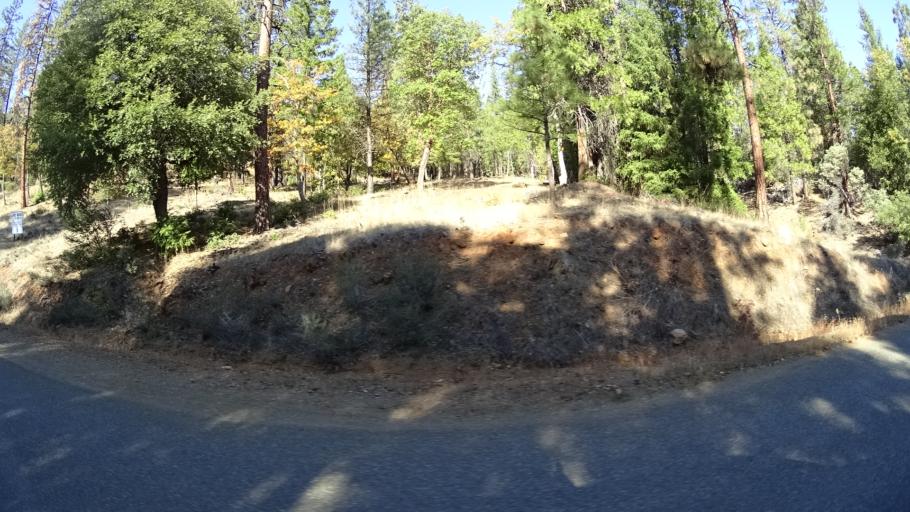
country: US
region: California
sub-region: Siskiyou County
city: Yreka
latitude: 41.7328
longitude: -123.0081
